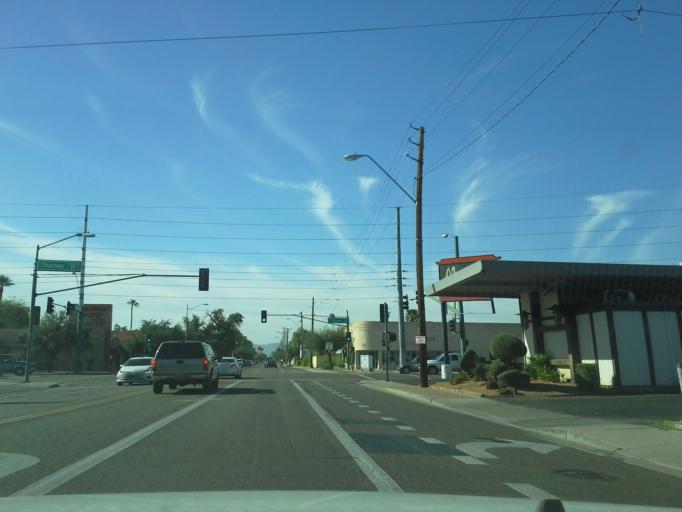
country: US
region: Arizona
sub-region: Maricopa County
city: Phoenix
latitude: 33.4811
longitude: -112.0914
